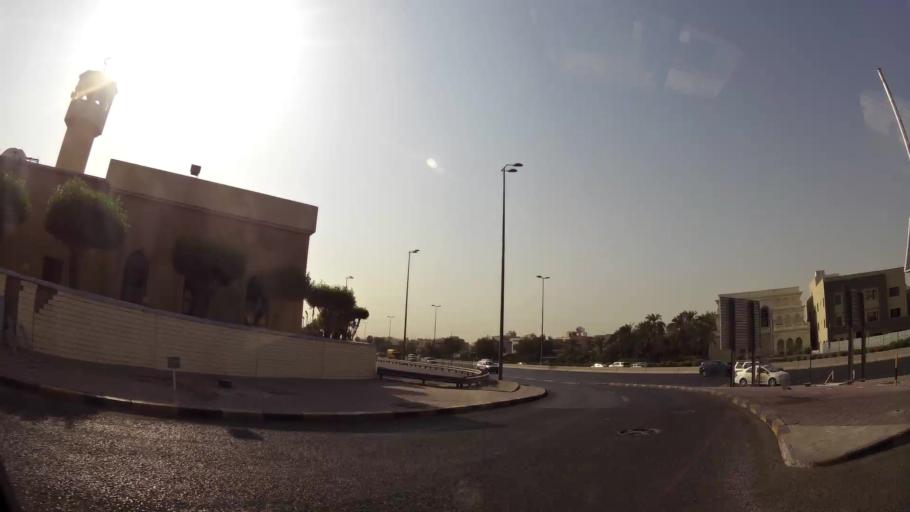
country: KW
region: Muhafazat Hawalli
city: Hawalli
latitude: 29.3373
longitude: 48.0032
